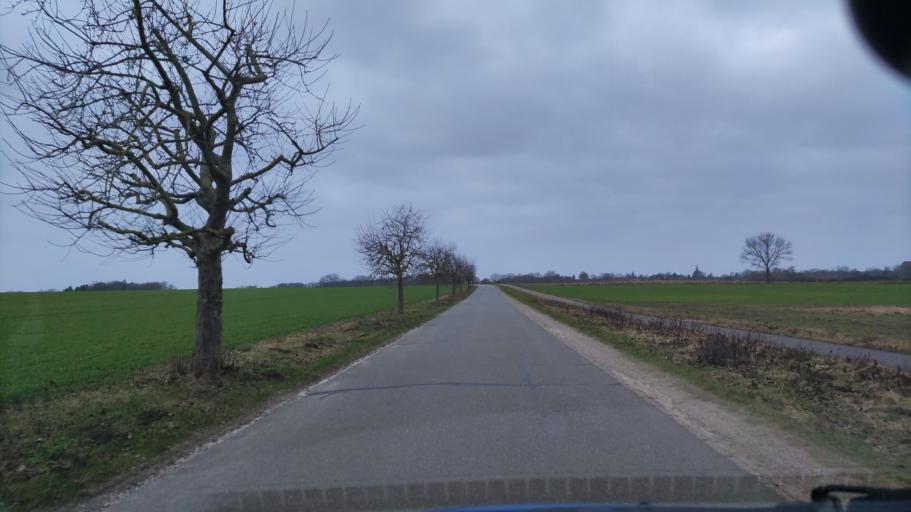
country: DE
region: Lower Saxony
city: Sudergellersen
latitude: 53.2070
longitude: 10.3141
